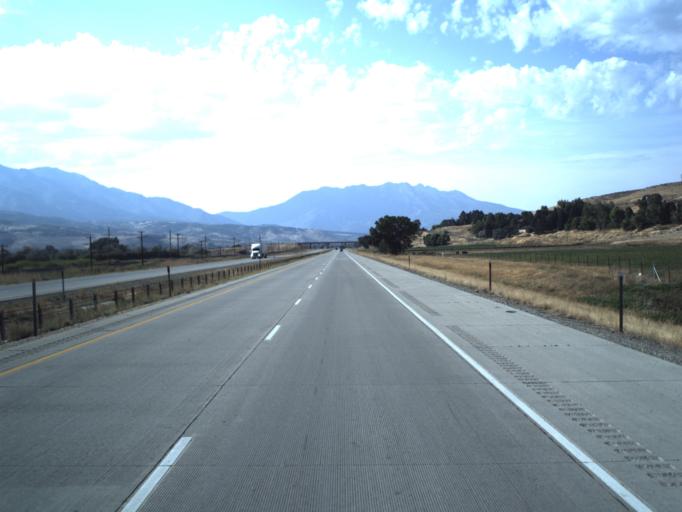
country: US
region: Utah
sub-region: Morgan County
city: Morgan
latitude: 41.0596
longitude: -111.7011
